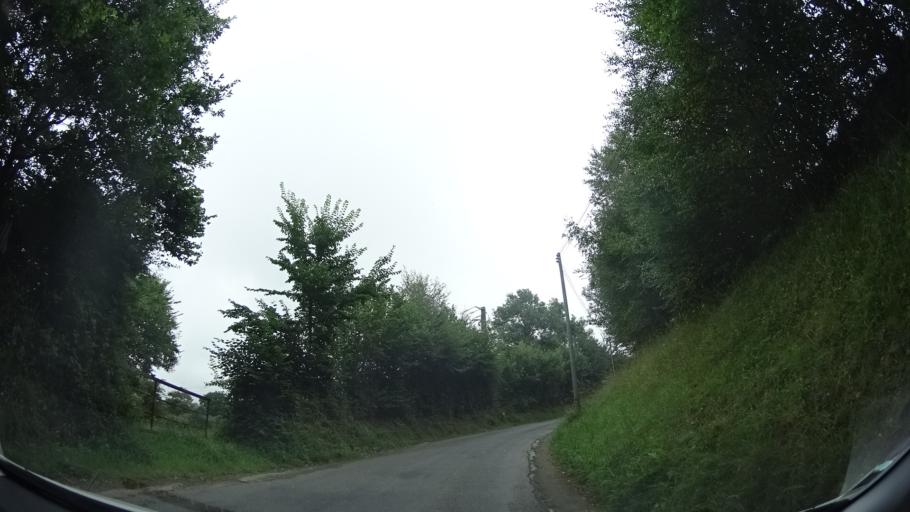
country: FR
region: Lower Normandy
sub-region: Departement de la Manche
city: Les Pieux
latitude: 49.5556
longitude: -1.7458
